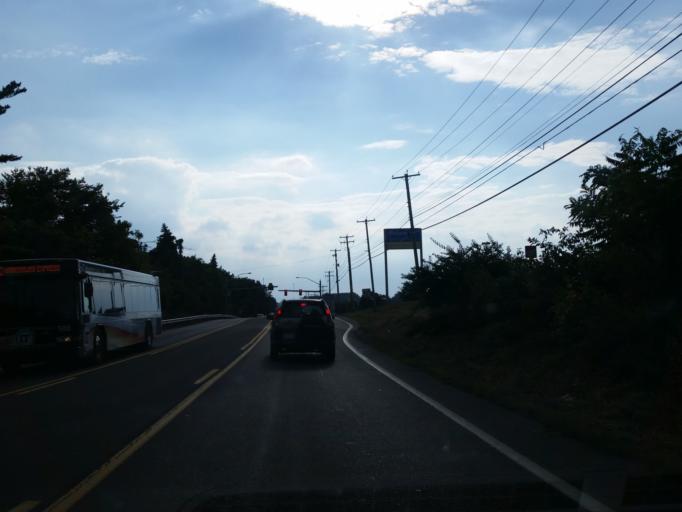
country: US
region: Pennsylvania
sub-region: Lebanon County
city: Palmyra
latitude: 40.3202
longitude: -76.5605
